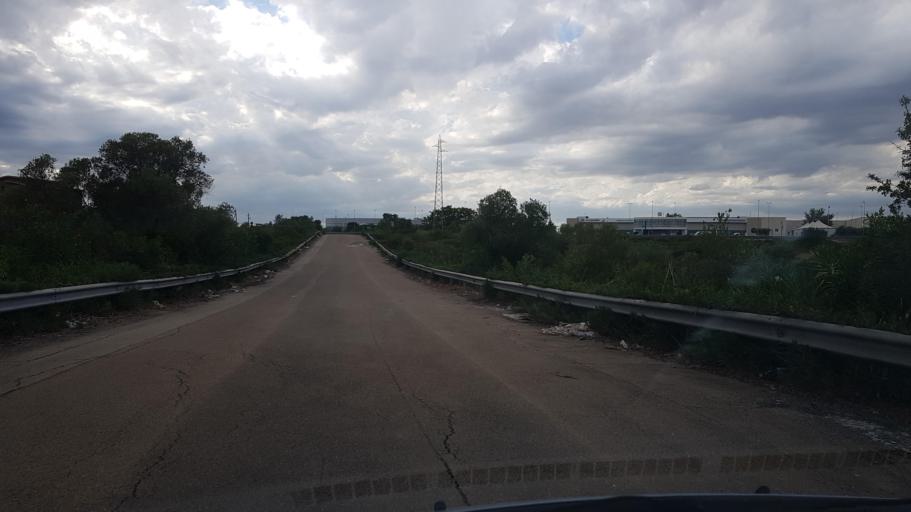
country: IT
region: Apulia
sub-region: Provincia di Taranto
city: Paolo VI
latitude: 40.5136
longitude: 17.2554
